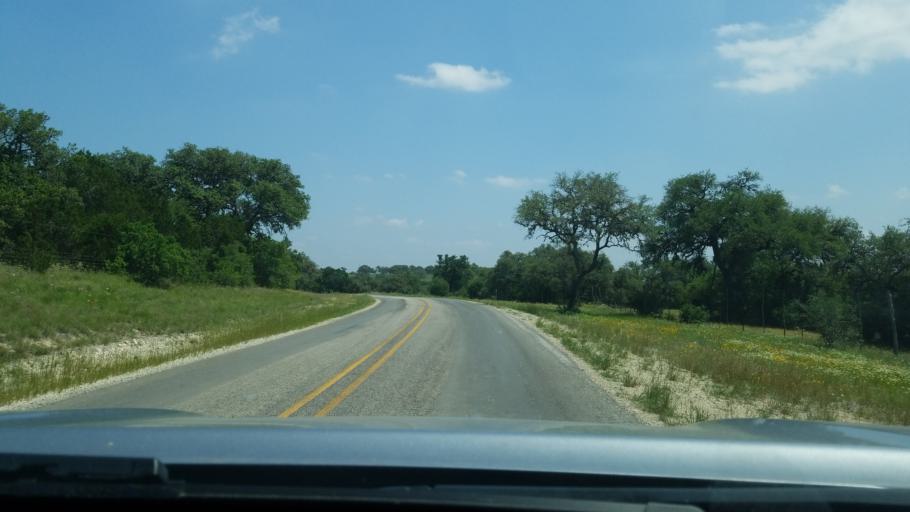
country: US
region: Texas
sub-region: Blanco County
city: Blanco
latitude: 29.9801
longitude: -98.5482
